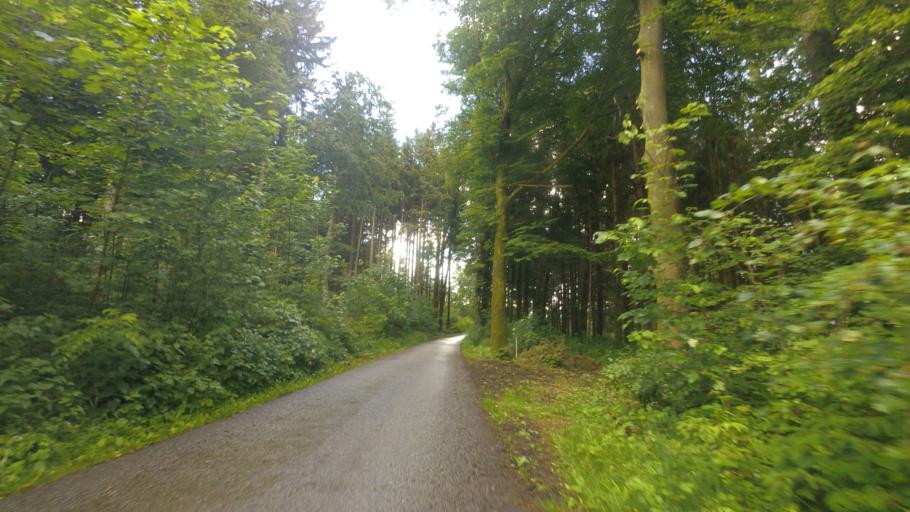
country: DE
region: Bavaria
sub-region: Upper Bavaria
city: Grabenstatt
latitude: 47.8287
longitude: 12.5425
